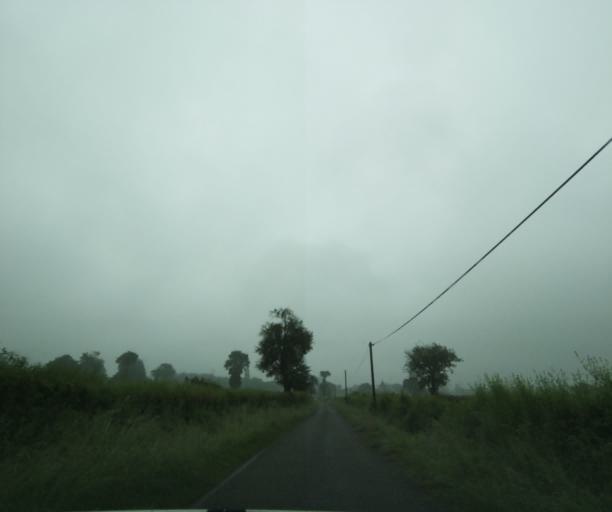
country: FR
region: Bourgogne
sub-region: Departement de Saone-et-Loire
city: Charolles
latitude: 46.4030
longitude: 4.2955
